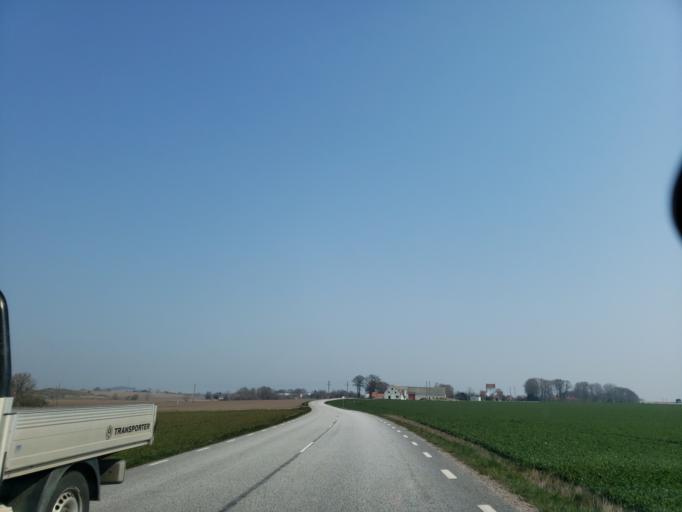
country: SE
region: Skane
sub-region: Simrishamns Kommun
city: Simrishamn
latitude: 55.4703
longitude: 14.2220
